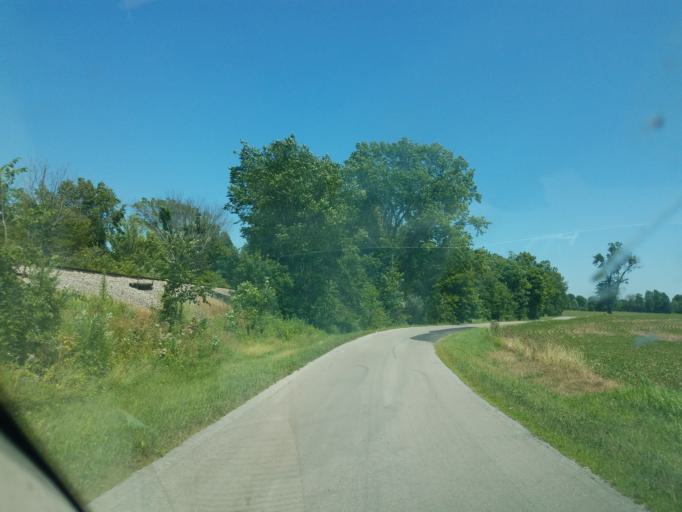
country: US
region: Ohio
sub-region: Hardin County
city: Forest
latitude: 40.8003
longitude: -83.5317
